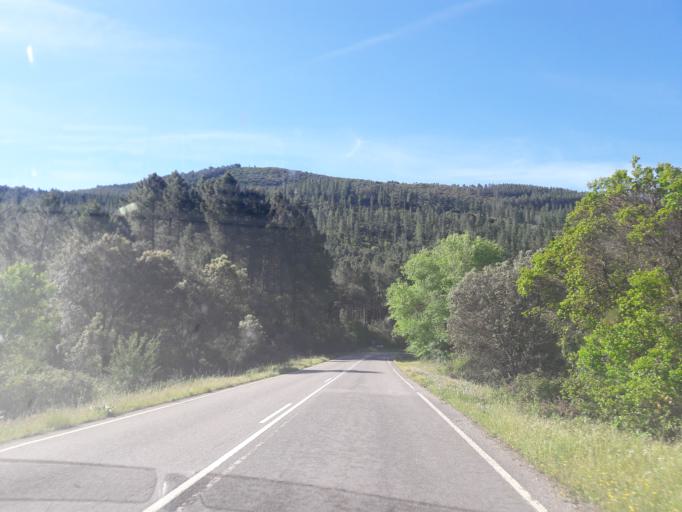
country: ES
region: Castille and Leon
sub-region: Provincia de Salamanca
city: Sotoserrano
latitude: 40.4077
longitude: -6.0524
